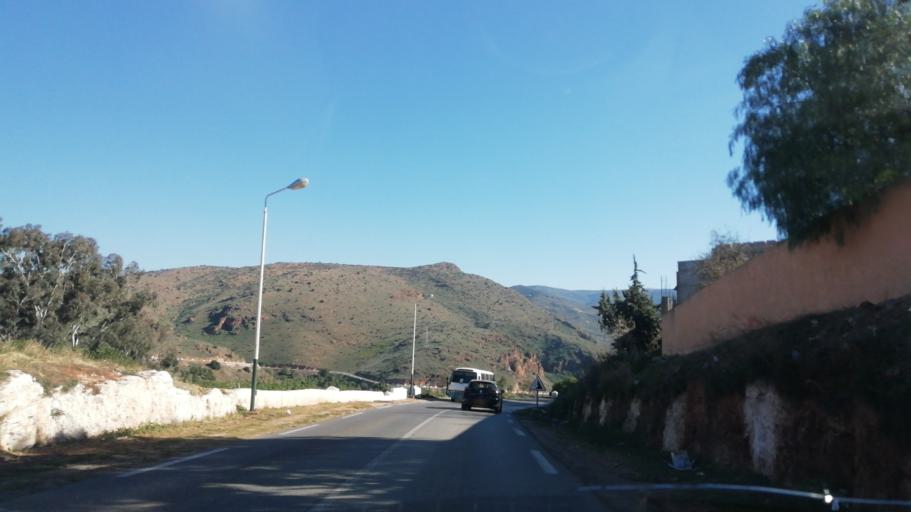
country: DZ
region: Tlemcen
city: Beni Mester
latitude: 34.8423
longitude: -1.4719
